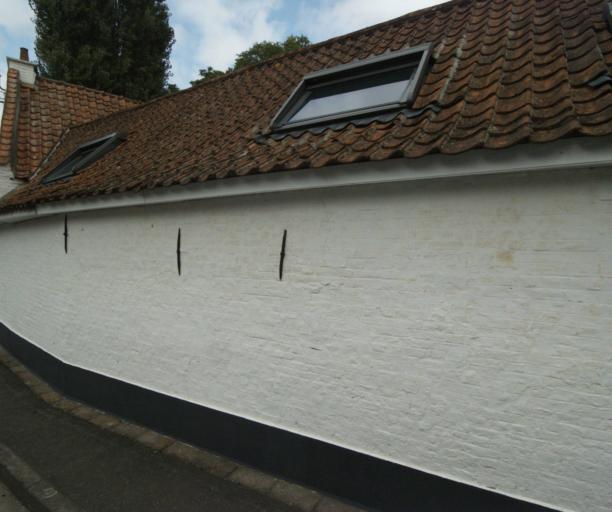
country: FR
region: Nord-Pas-de-Calais
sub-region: Departement du Nord
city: Gruson
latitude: 50.5950
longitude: 3.2020
